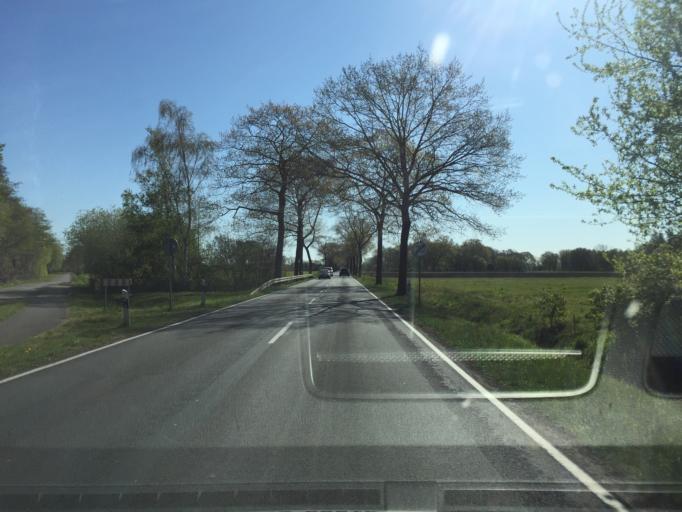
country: DE
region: Lower Saxony
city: Wagenfeld
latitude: 52.5478
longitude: 8.6024
